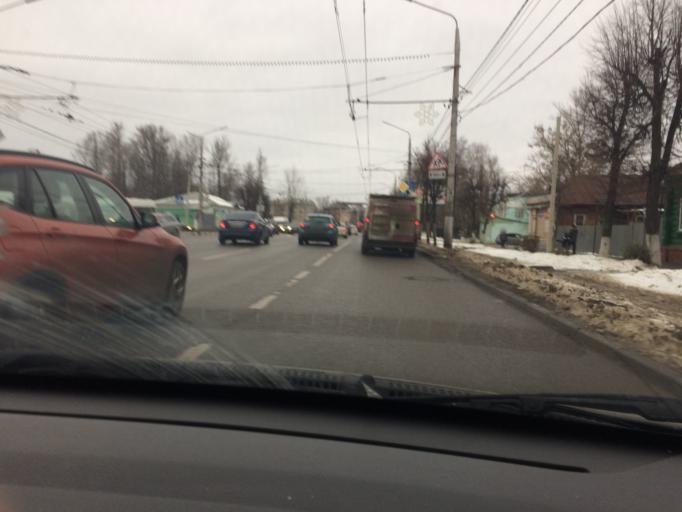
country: RU
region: Tula
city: Tula
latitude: 54.2248
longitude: 37.6282
